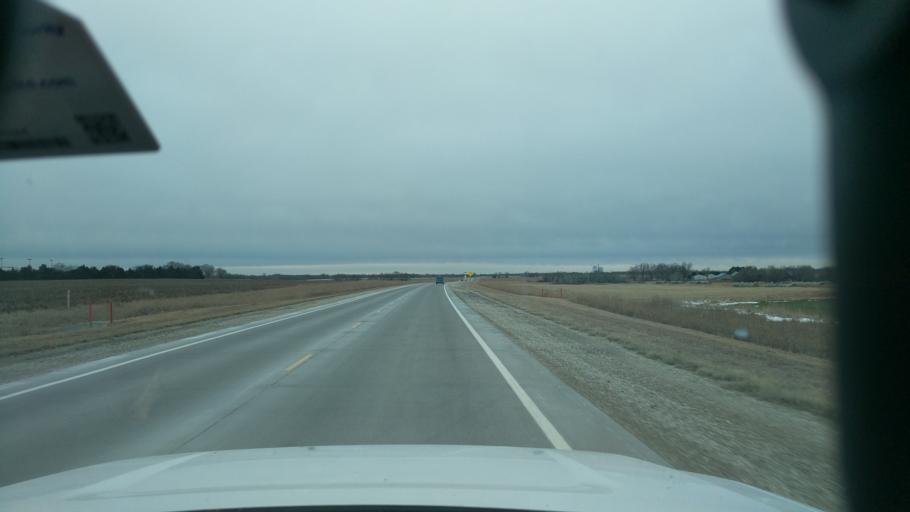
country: US
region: Kansas
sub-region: Dickinson County
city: Herington
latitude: 38.5286
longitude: -96.9564
